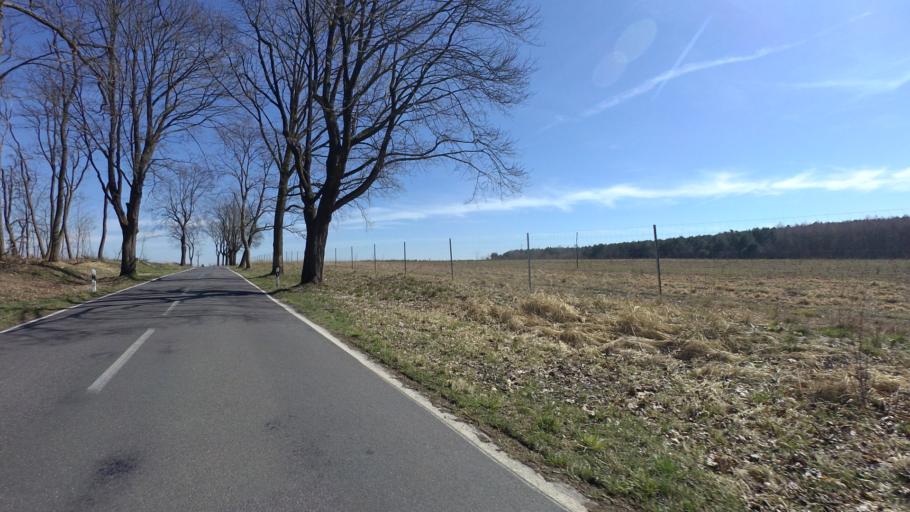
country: DE
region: Brandenburg
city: Munchehofe
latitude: 52.1600
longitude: 13.9034
